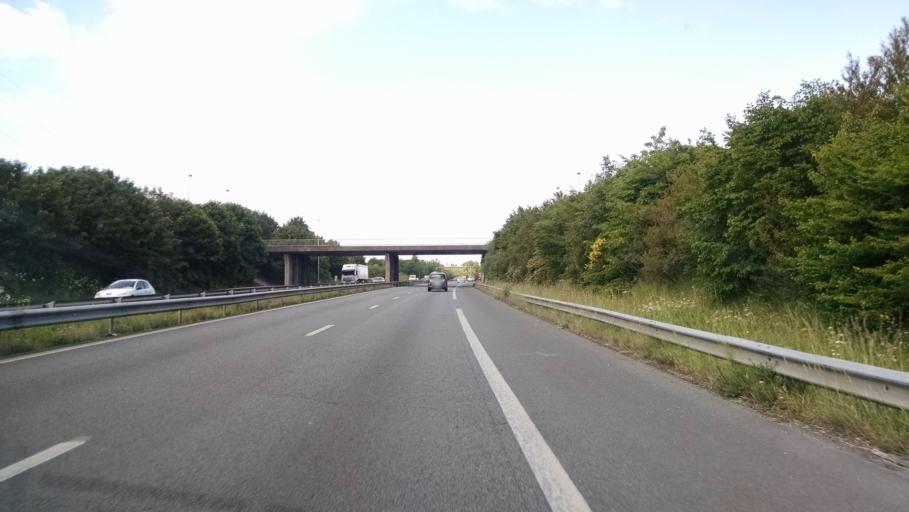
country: FR
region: Pays de la Loire
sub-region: Departement de la Loire-Atlantique
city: Les Sorinieres
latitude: 47.1592
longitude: -1.5404
